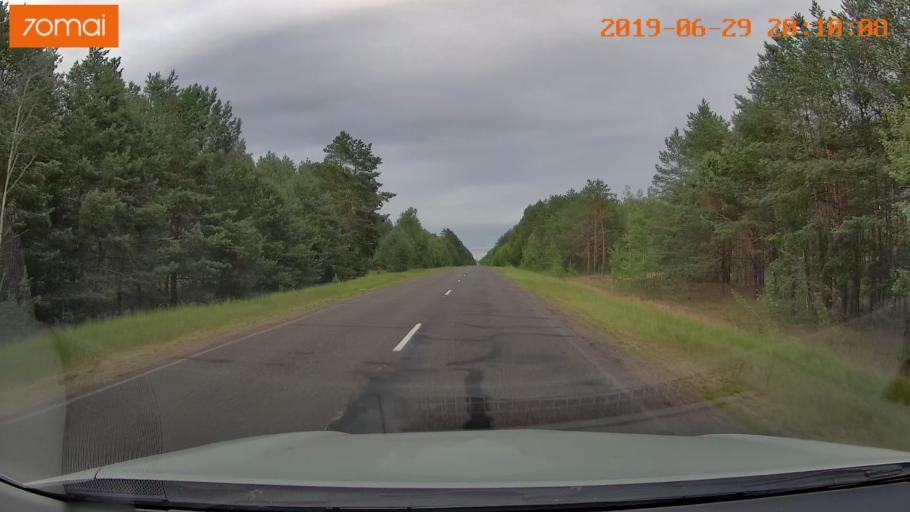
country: BY
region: Brest
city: Lahishyn
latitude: 52.3518
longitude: 26.0862
